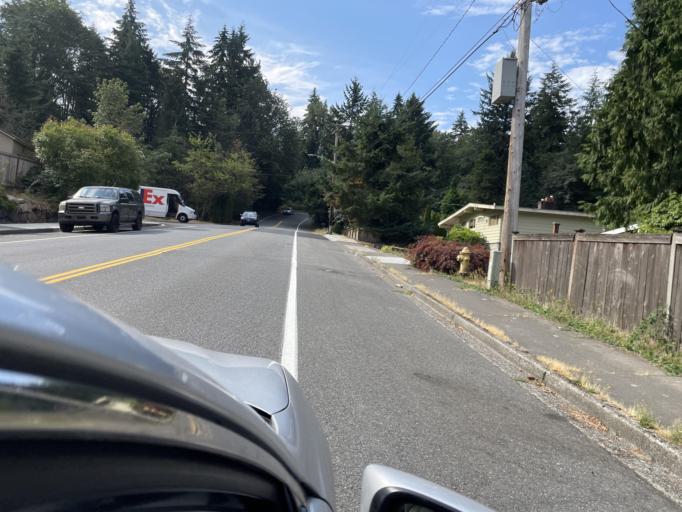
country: US
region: Washington
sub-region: King County
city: Eastgate
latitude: 47.5682
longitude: -122.1422
